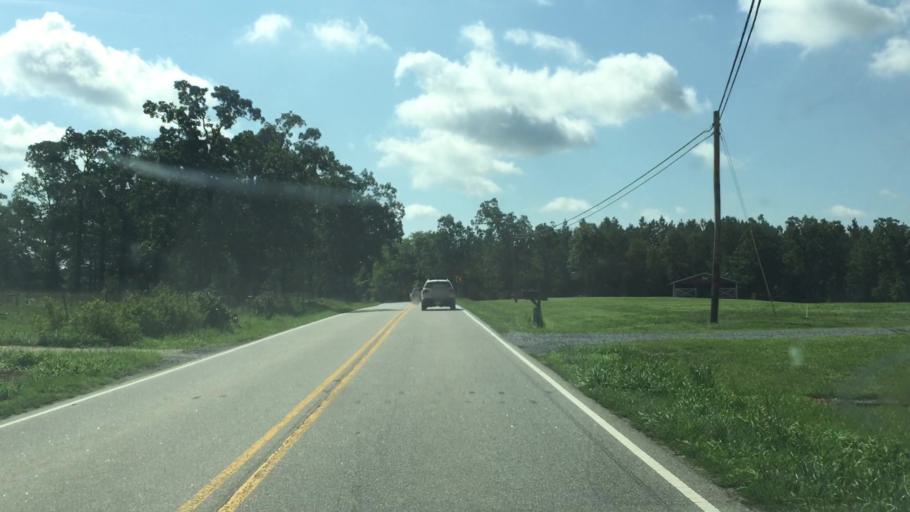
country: US
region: North Carolina
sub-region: Anson County
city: Polkton
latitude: 35.0324
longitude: -80.2431
